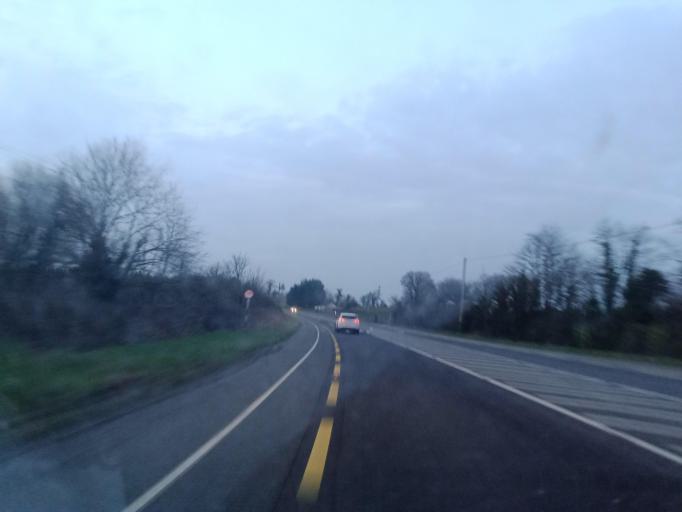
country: IE
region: Leinster
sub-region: Laois
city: Abbeyleix
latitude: 52.8739
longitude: -7.3621
